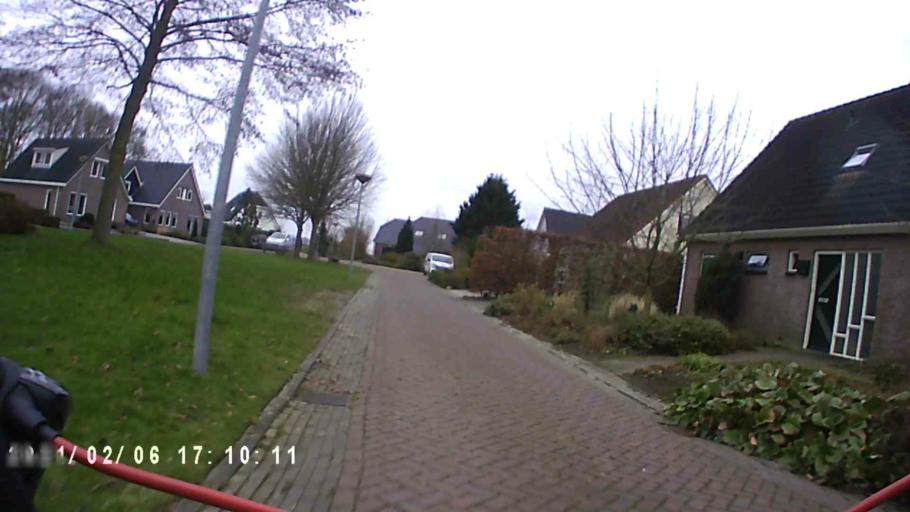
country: NL
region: Groningen
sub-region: Gemeente Appingedam
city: Appingedam
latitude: 53.4176
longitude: 6.7675
